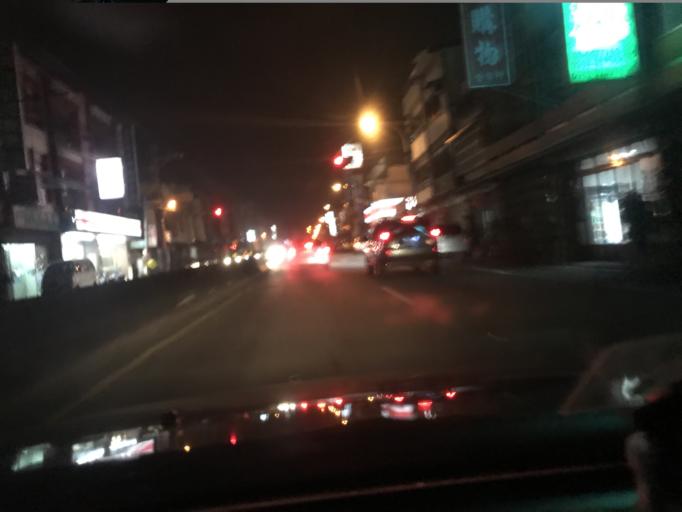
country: TW
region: Taiwan
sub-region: Hsinchu
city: Zhubei
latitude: 24.8035
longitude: 121.0505
